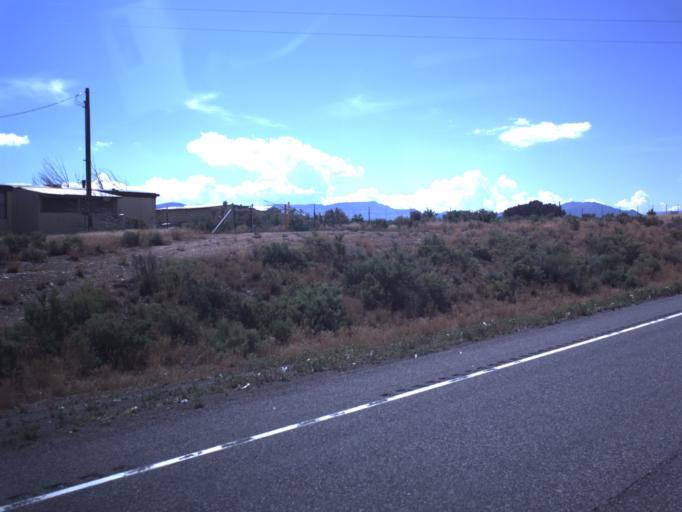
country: US
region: Utah
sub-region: Piute County
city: Junction
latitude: 38.4101
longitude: -112.2314
